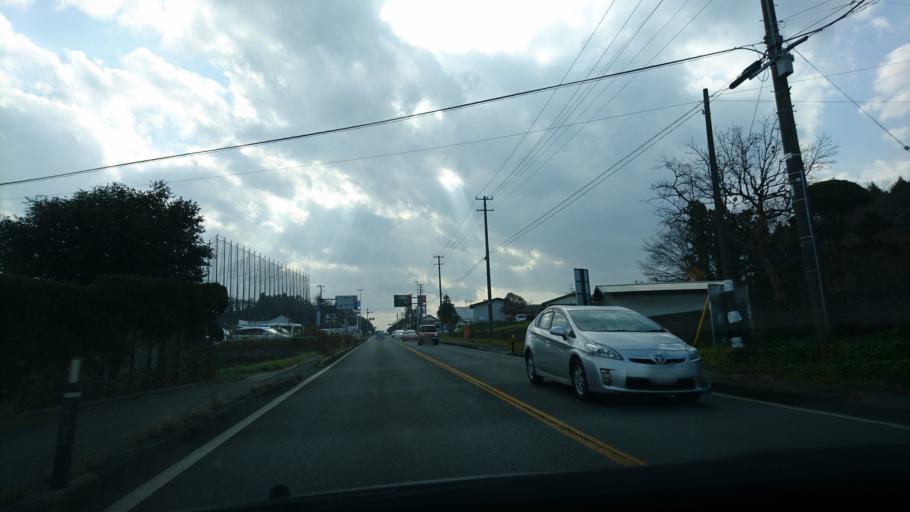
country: JP
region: Iwate
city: Mizusawa
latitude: 39.0343
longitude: 141.1181
